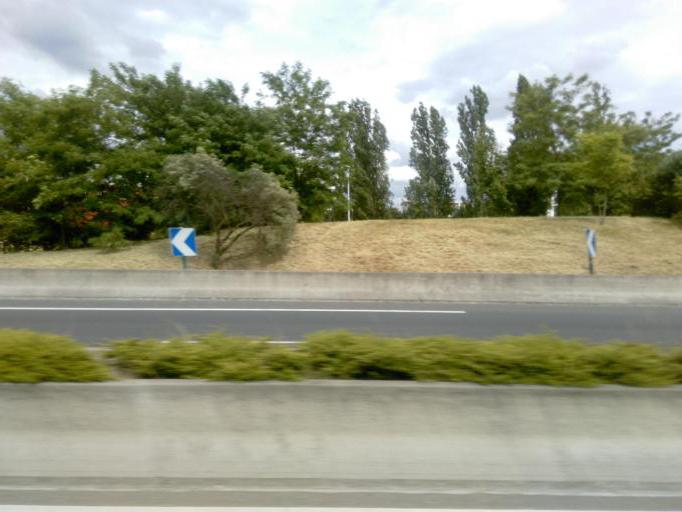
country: FR
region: Ile-de-France
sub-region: Departement du Val-d'Oise
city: Pontoise
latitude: 49.0644
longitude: 2.0868
